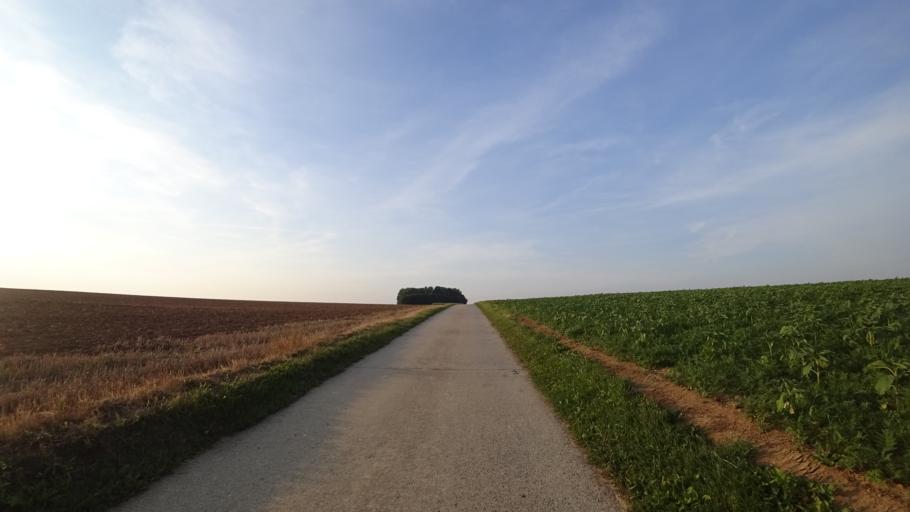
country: BE
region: Wallonia
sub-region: Province du Brabant Wallon
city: Walhain-Saint-Paul
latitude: 50.6160
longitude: 4.6812
